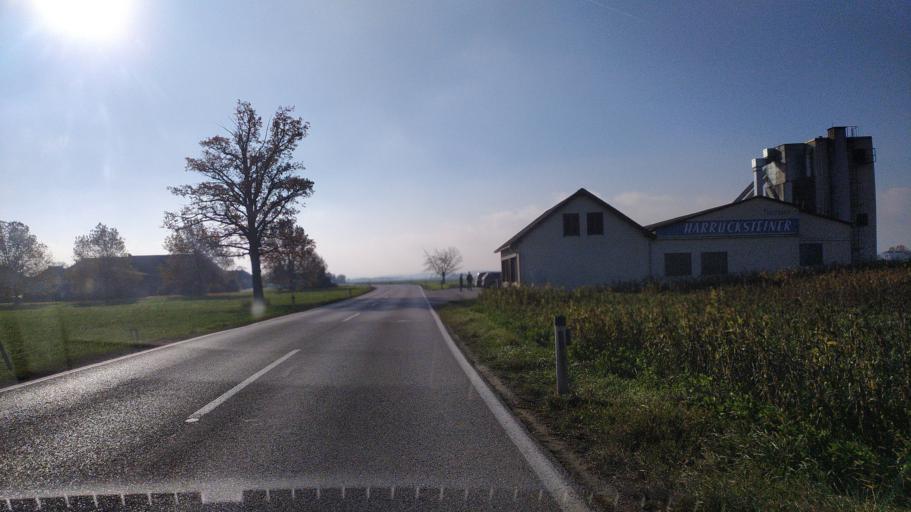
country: AT
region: Upper Austria
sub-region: Politischer Bezirk Perg
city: Perg
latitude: 48.2327
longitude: 14.6229
